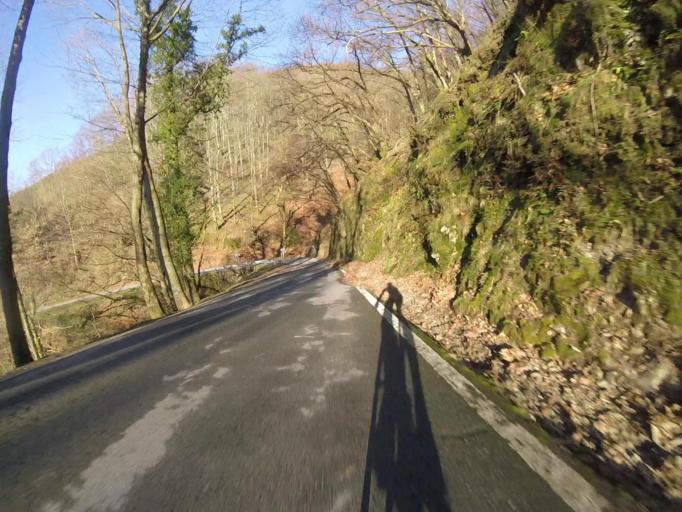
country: ES
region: Navarre
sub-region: Provincia de Navarra
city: Lesaka
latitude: 43.2666
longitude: -1.7671
